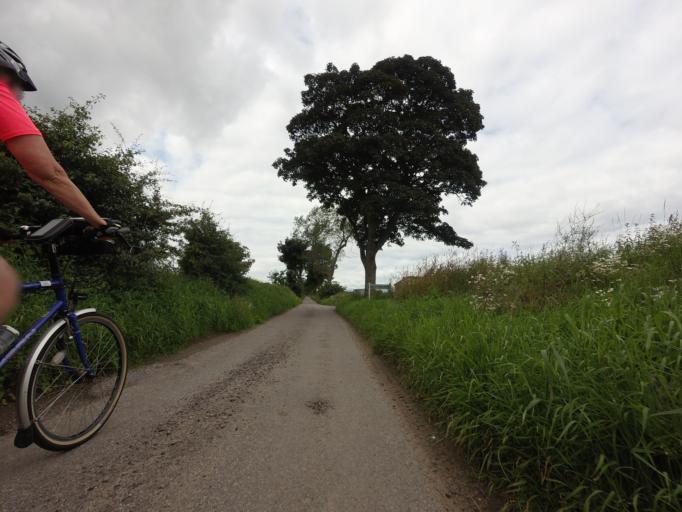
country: GB
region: Scotland
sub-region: Moray
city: Forres
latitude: 57.6128
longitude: -3.6442
